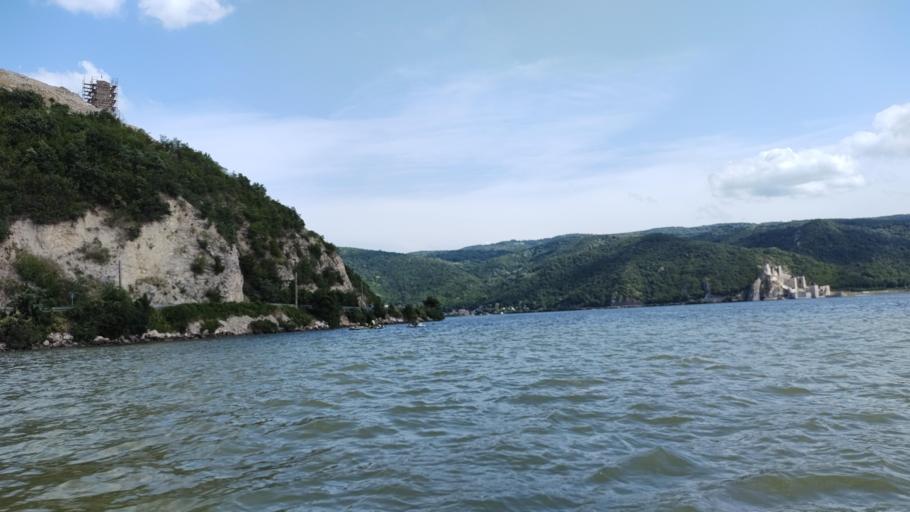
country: RO
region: Caras-Severin
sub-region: Comuna Pescari
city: Coronini
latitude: 44.6742
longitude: 21.6781
